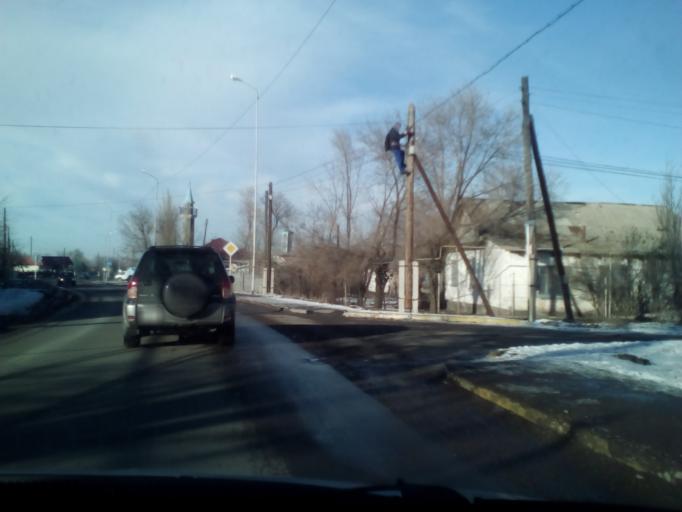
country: KZ
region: Almaty Oblysy
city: Burunday
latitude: 43.1755
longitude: 76.4151
